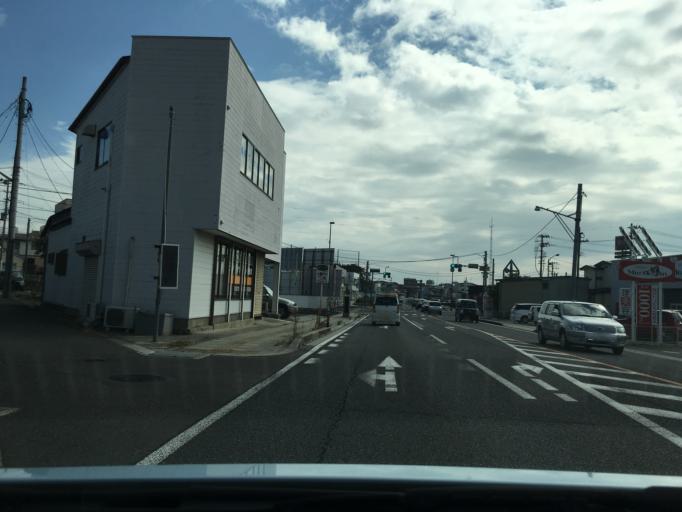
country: JP
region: Fukushima
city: Koriyama
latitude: 37.3846
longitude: 140.3596
